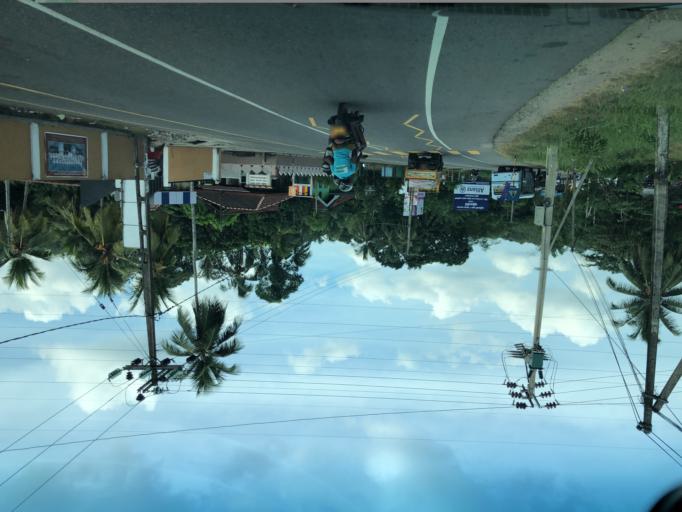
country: LK
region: Western
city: Horawala Junction
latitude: 6.5237
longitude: 80.1048
